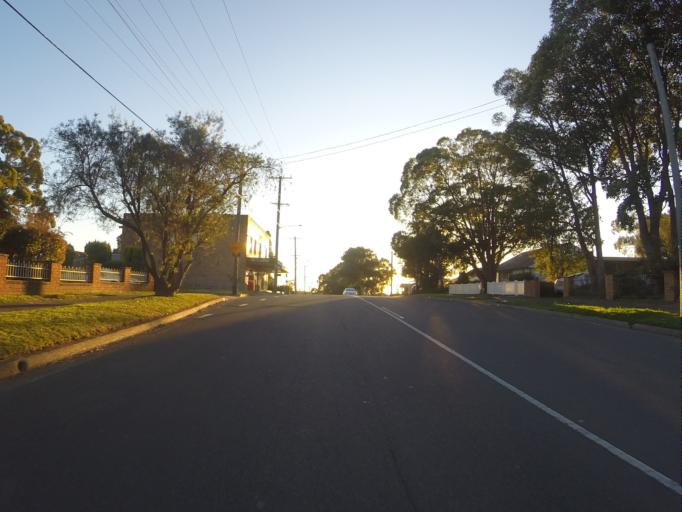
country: AU
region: New South Wales
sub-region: Sutherland Shire
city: Engadine
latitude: -34.0597
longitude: 151.0130
